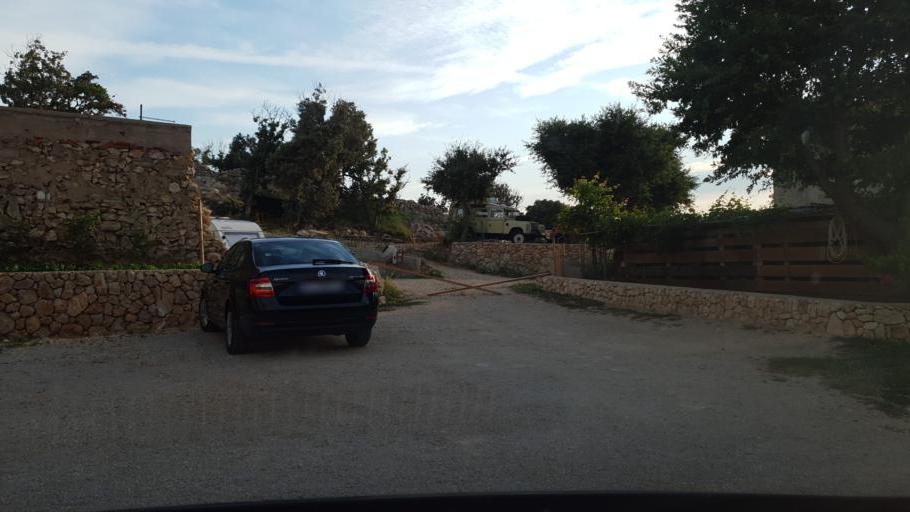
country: HR
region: Primorsko-Goranska
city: Punat
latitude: 44.9523
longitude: 14.6905
